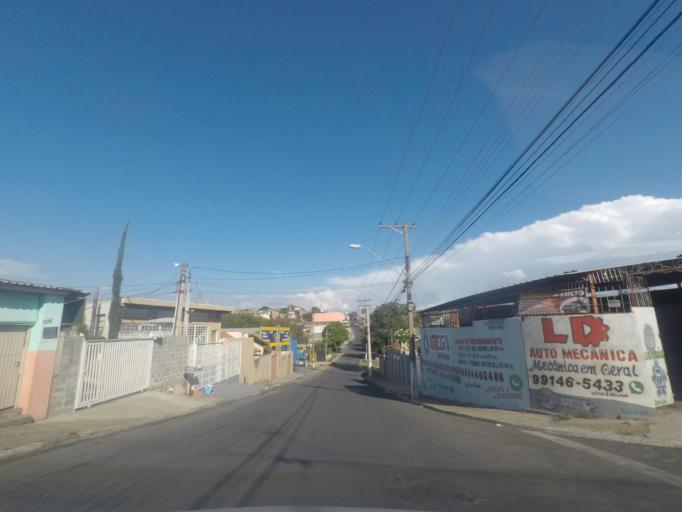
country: BR
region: Sao Paulo
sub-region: Sumare
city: Sumare
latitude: -22.8122
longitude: -47.2637
